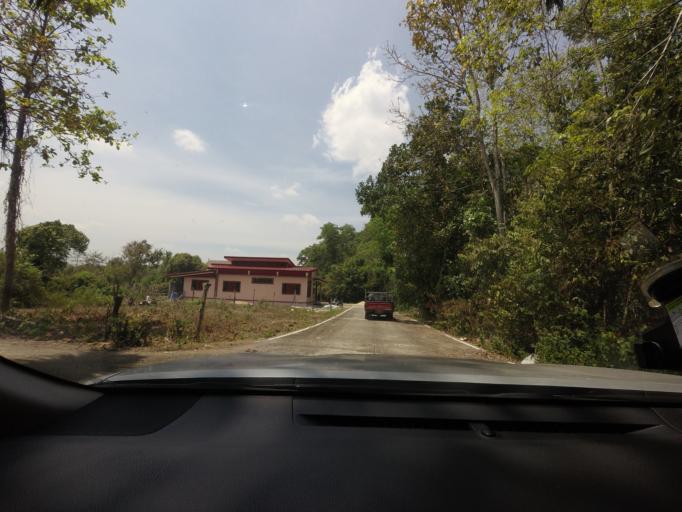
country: TH
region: Narathiwat
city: Rueso
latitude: 6.3864
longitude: 101.5099
